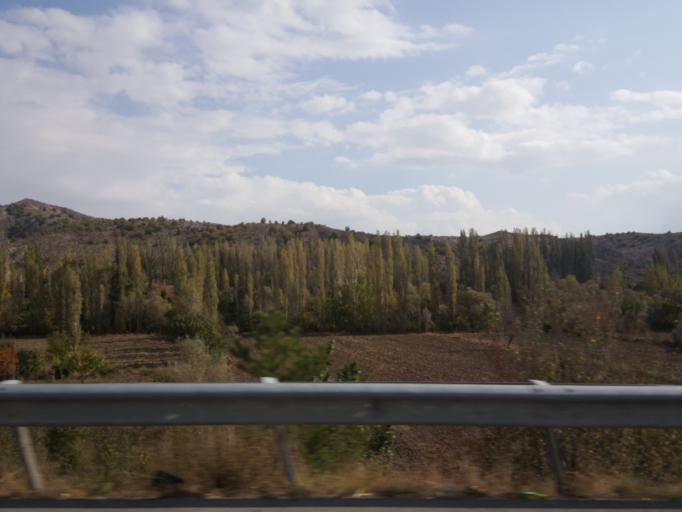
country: TR
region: Corum
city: Sungurlu
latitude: 40.1935
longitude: 34.5051
